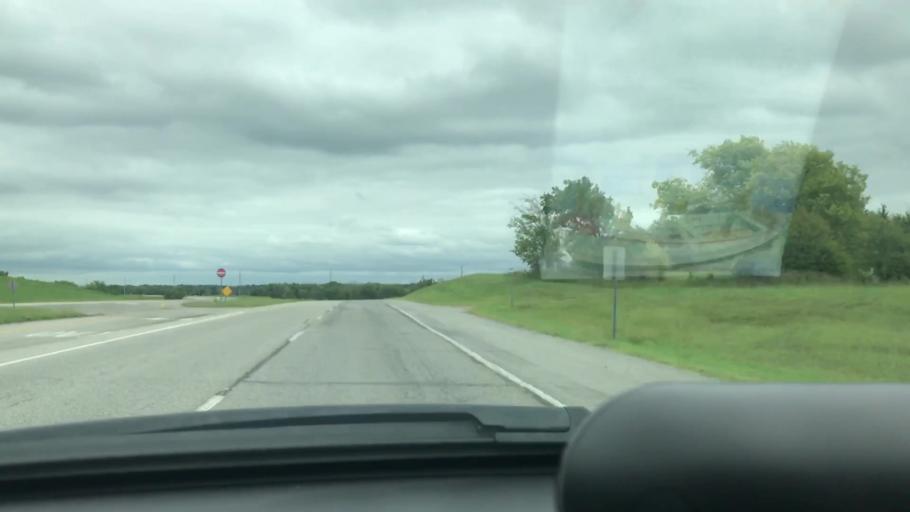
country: US
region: Oklahoma
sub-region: Wagoner County
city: Wagoner
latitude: 35.9913
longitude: -95.3719
